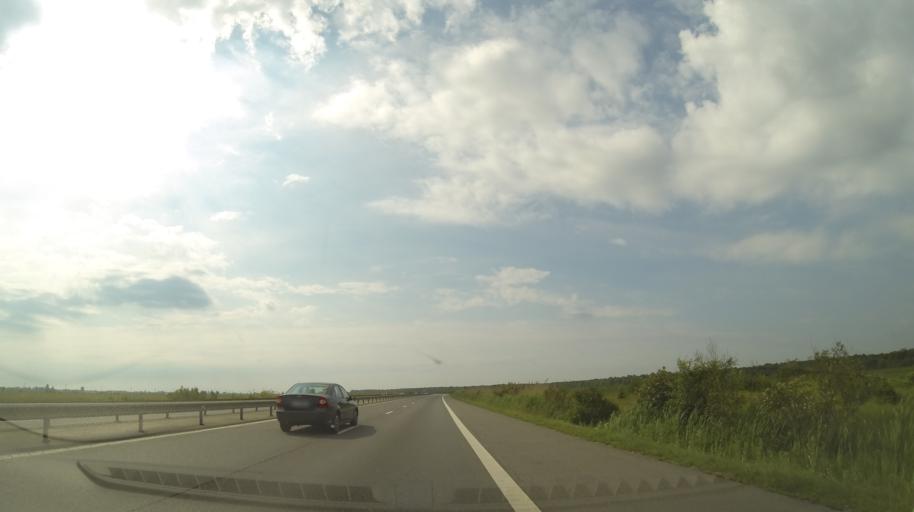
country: RO
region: Dambovita
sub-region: Comuna Corbii Mari
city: Grozavesti
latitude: 44.5969
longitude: 25.4598
